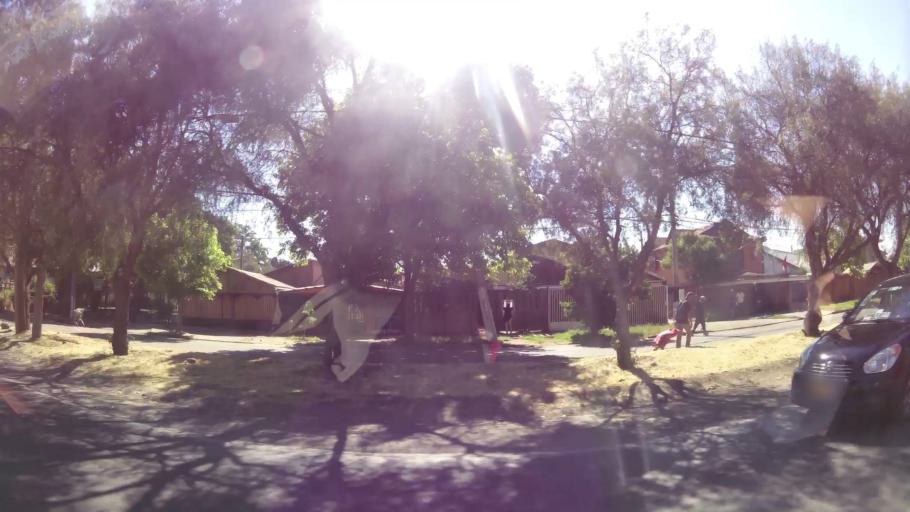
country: CL
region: Santiago Metropolitan
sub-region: Provincia de Maipo
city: San Bernardo
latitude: -33.6103
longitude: -70.6837
